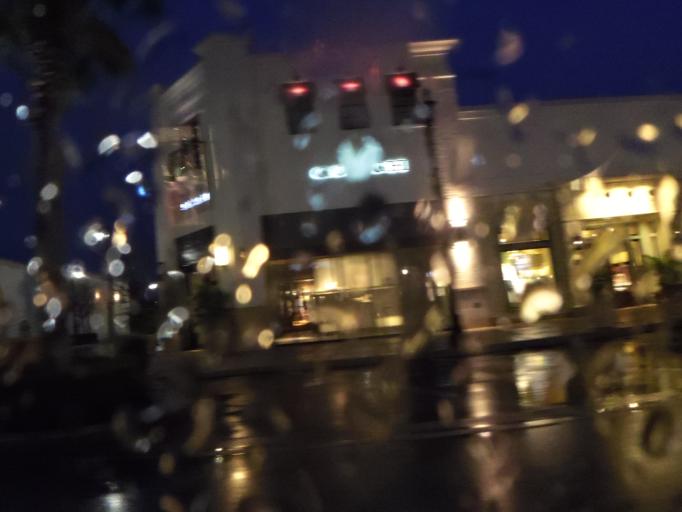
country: US
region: Florida
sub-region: Duval County
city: Jacksonville Beach
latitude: 30.2545
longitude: -81.5254
